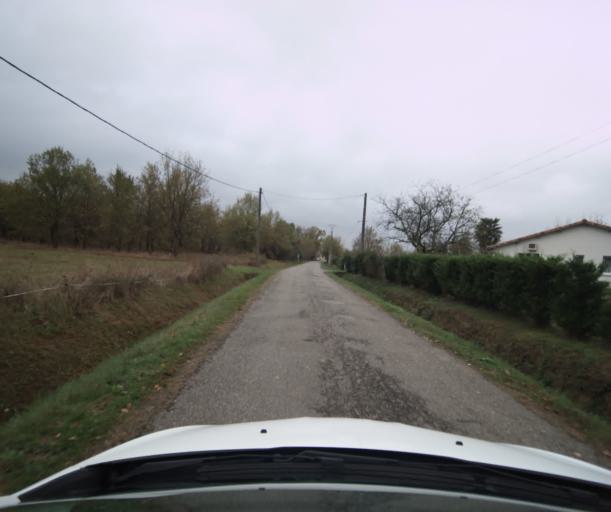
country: FR
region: Midi-Pyrenees
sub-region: Departement du Tarn-et-Garonne
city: Moissac
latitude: 44.0769
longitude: 1.1490
